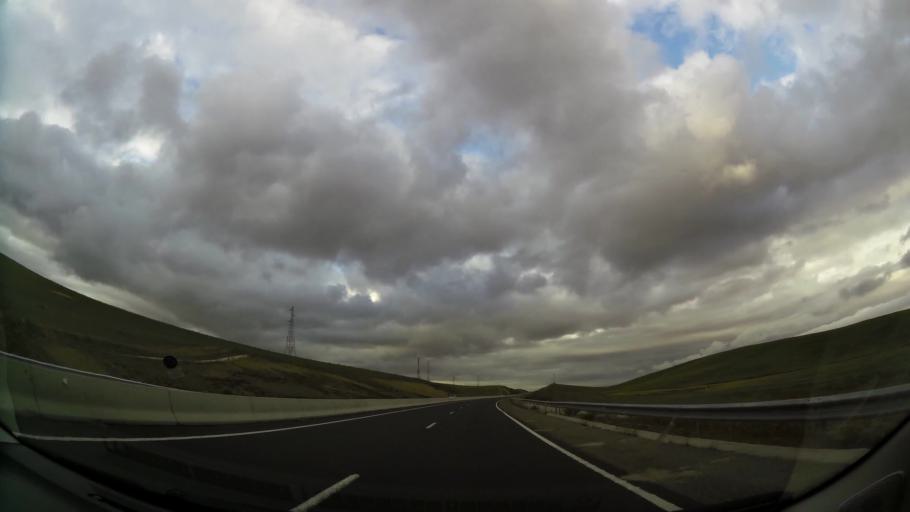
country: MA
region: Taza-Al Hoceima-Taounate
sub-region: Taza
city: Taza
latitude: 34.2677
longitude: -3.8392
